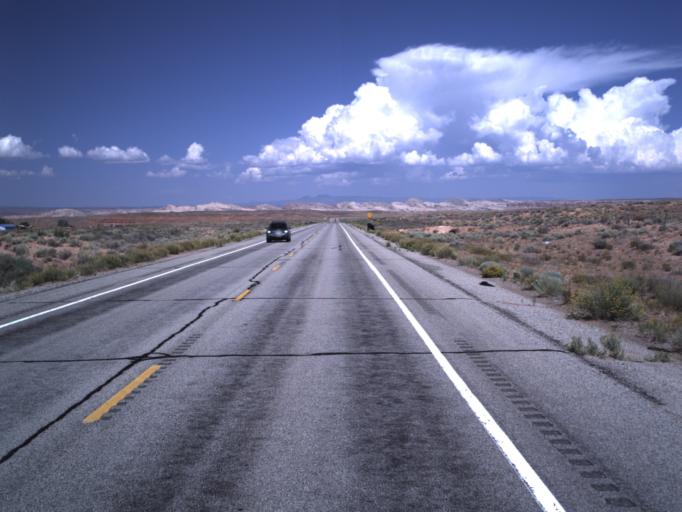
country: US
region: Utah
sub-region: San Juan County
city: Blanding
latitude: 37.2090
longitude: -109.6093
